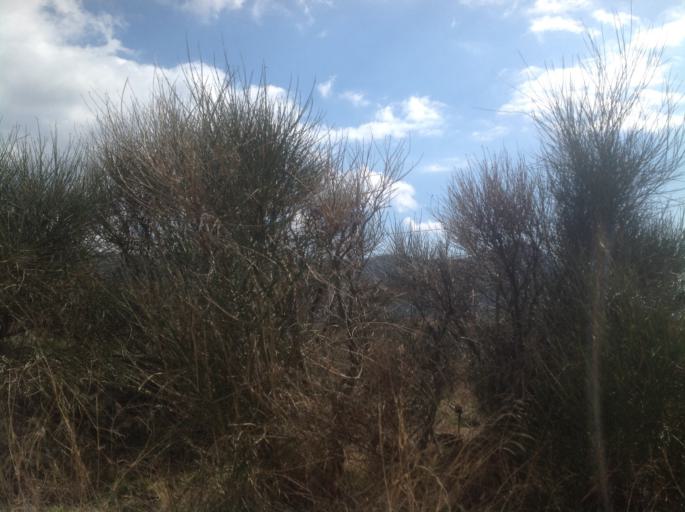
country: IT
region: Calabria
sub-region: Provincia di Cosenza
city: Civita
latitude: 39.8423
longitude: 16.3084
